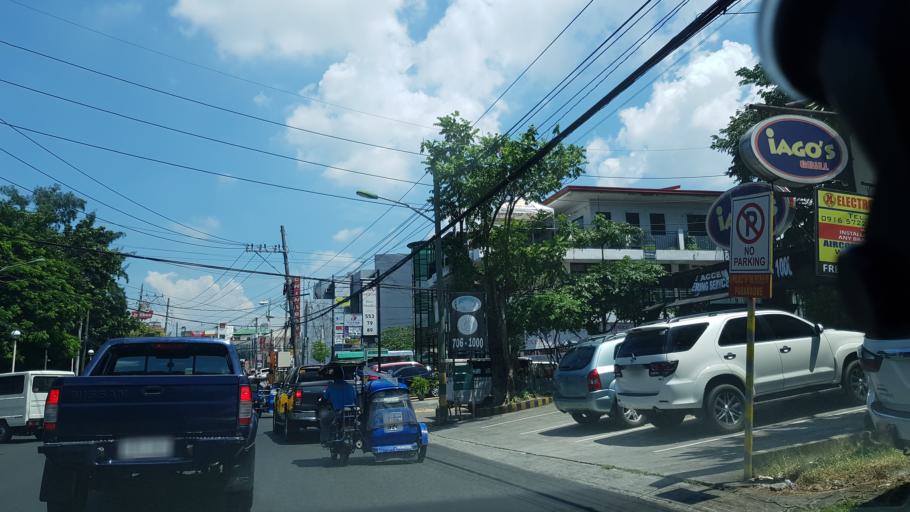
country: PH
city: Sambayanihan People's Village
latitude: 14.4450
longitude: 121.0263
